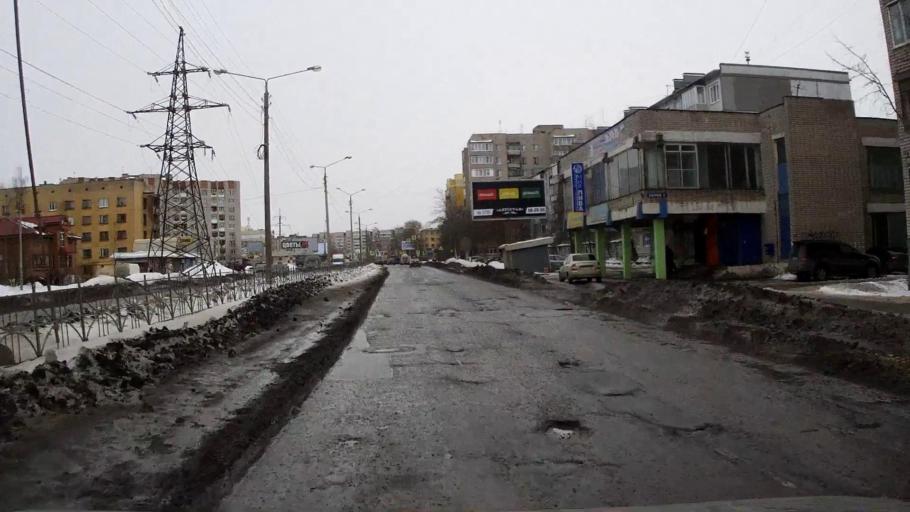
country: RU
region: Vologda
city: Vologda
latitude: 59.2159
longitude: 39.9224
